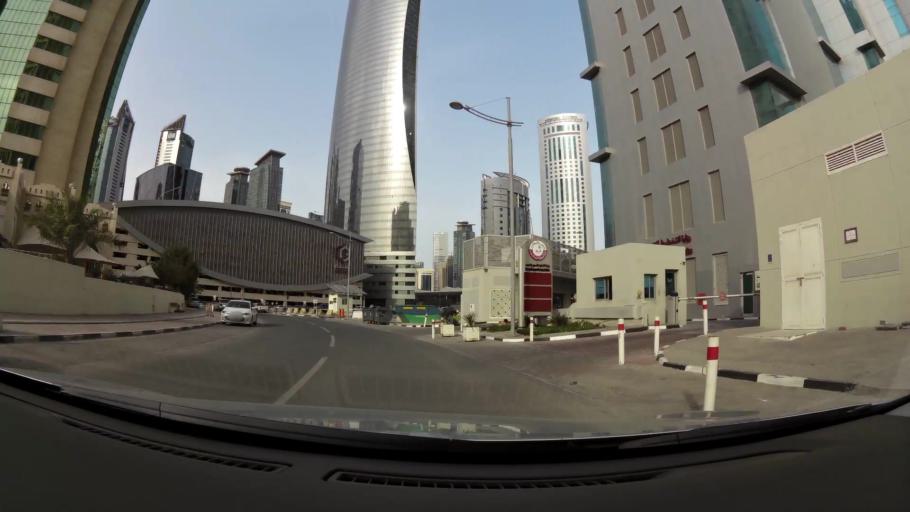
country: QA
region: Baladiyat ad Dawhah
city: Doha
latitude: 25.3201
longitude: 51.5257
